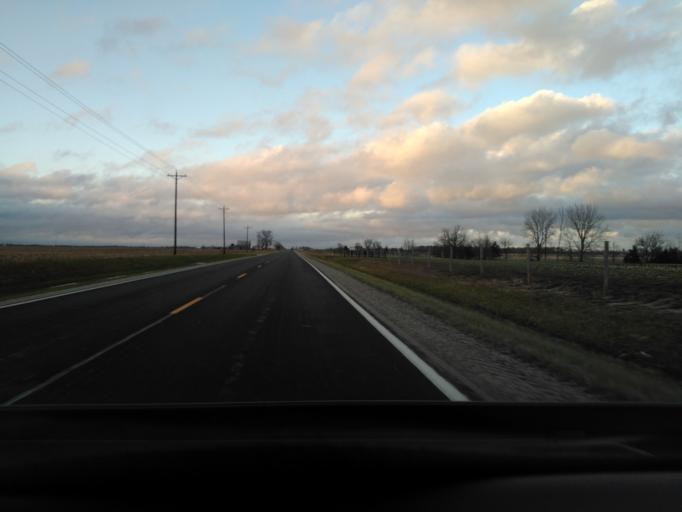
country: US
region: Illinois
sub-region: Effingham County
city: Altamont
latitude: 38.9950
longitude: -88.7487
